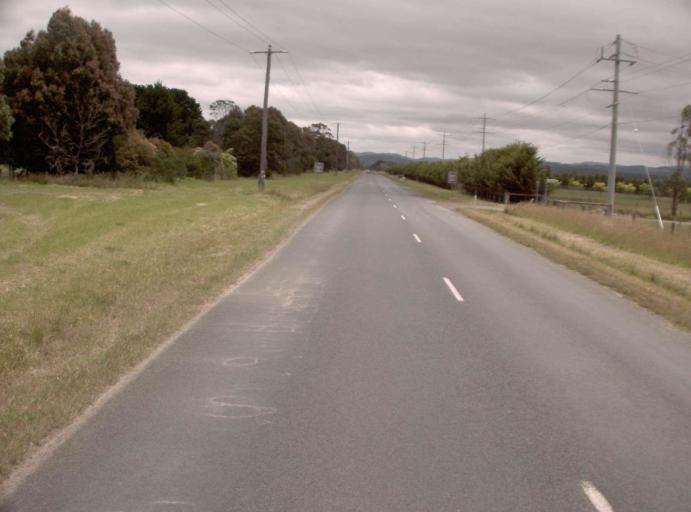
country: AU
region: Victoria
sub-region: Latrobe
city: Traralgon
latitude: -38.5552
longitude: 146.6689
